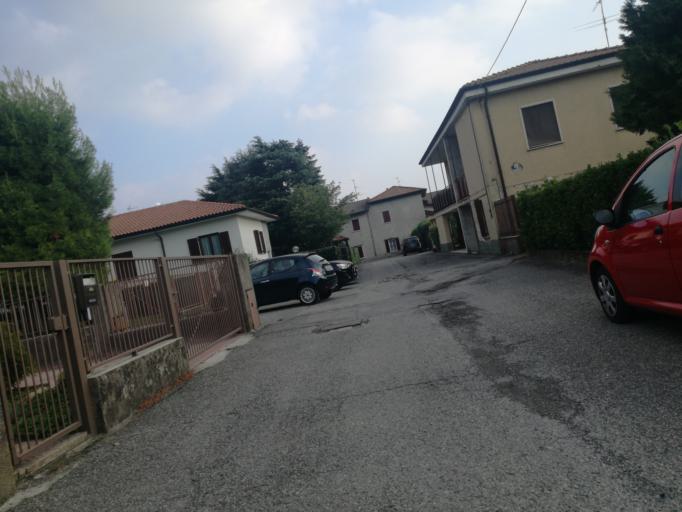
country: IT
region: Lombardy
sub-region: Provincia di Monza e Brianza
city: Porto d'Adda
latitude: 45.6489
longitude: 9.4675
